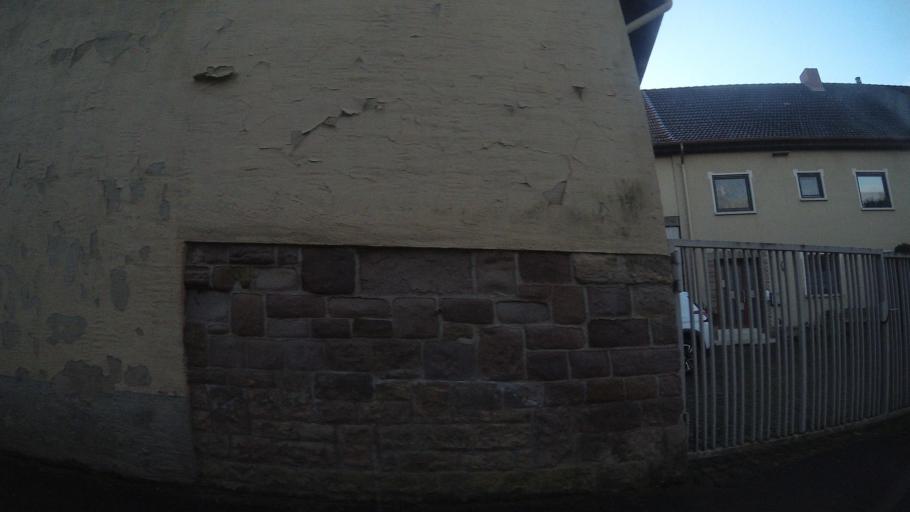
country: DE
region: Rheinland-Pfalz
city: Niedermoschel
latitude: 49.7322
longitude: 7.7922
